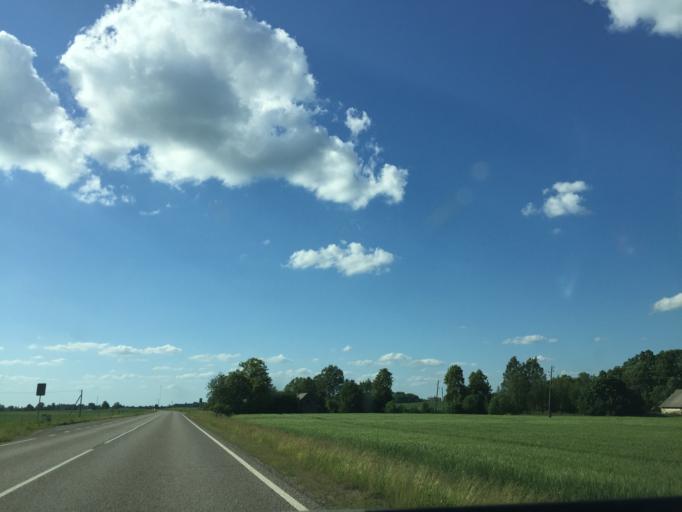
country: LV
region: Kandava
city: Kandava
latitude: 56.9090
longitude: 22.8393
